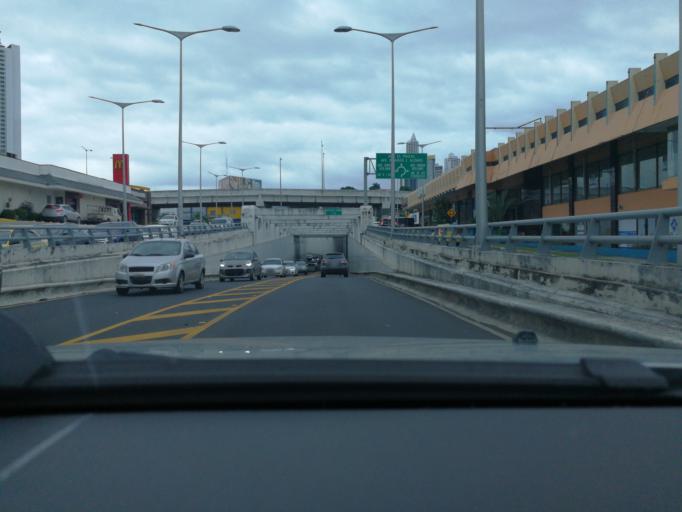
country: PA
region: Panama
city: Panama
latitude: 8.9953
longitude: -79.5268
